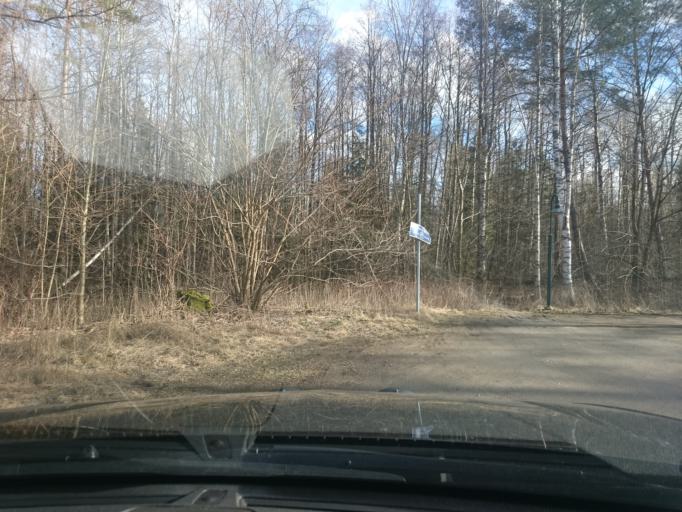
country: SE
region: Joenkoeping
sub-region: Vetlanda Kommun
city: Vetlanda
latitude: 57.4136
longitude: 15.0925
